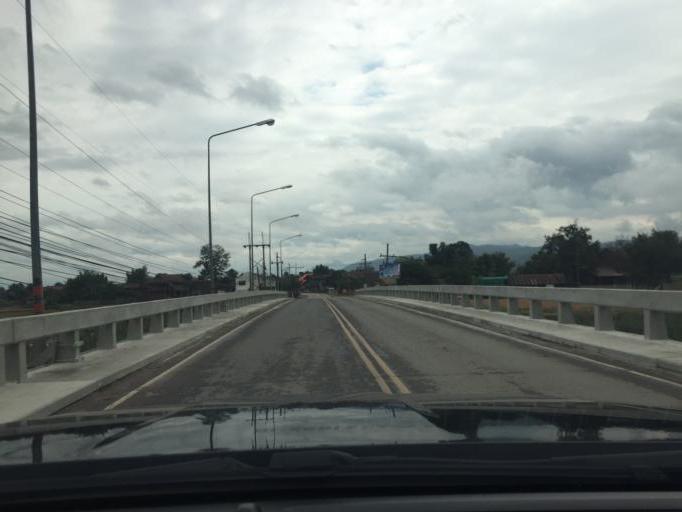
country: TH
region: Phayao
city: Pong
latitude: 19.1682
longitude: 100.2846
